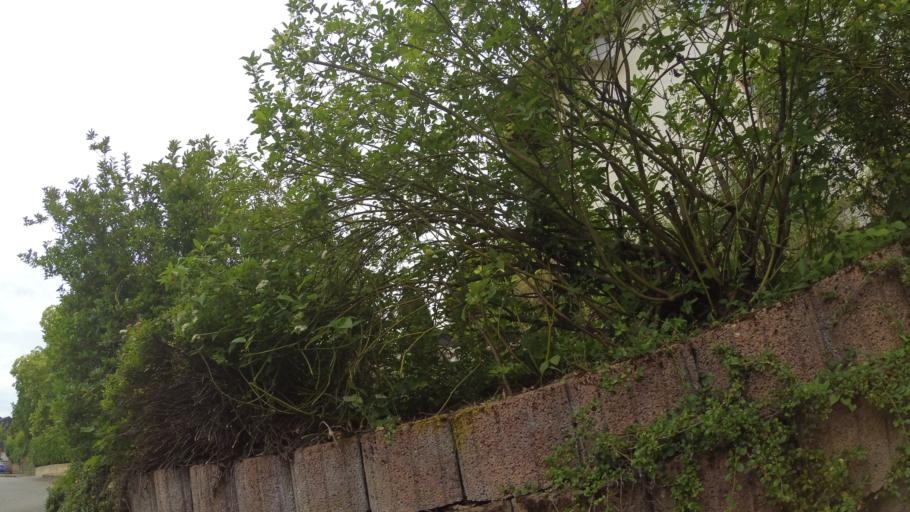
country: DE
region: Saarland
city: Wallerfangen
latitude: 49.3278
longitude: 6.6973
